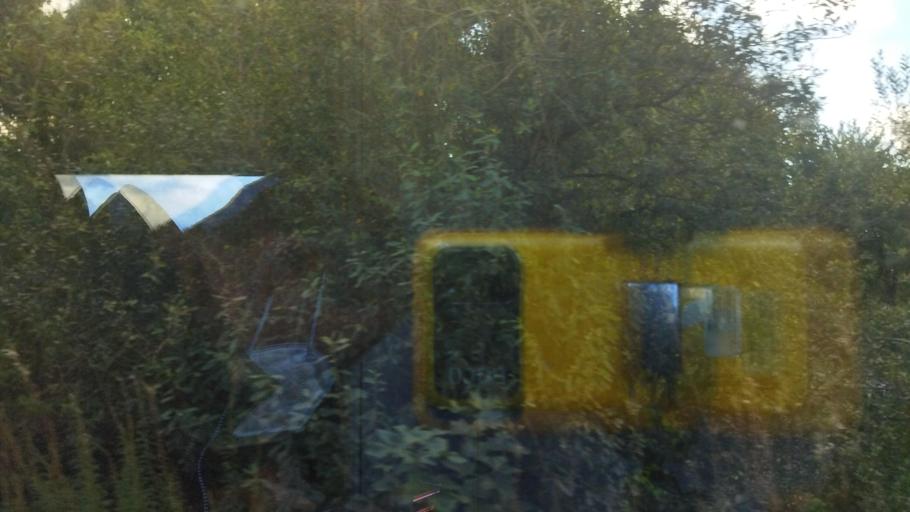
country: DE
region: Lower Saxony
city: Emden
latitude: 53.3405
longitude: 7.2712
